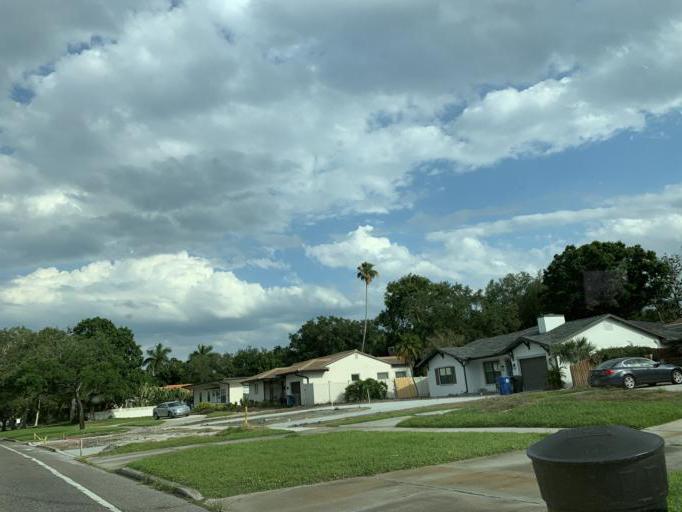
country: US
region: Florida
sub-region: Pinellas County
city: Saint Petersburg
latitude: 27.7952
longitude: -82.6186
